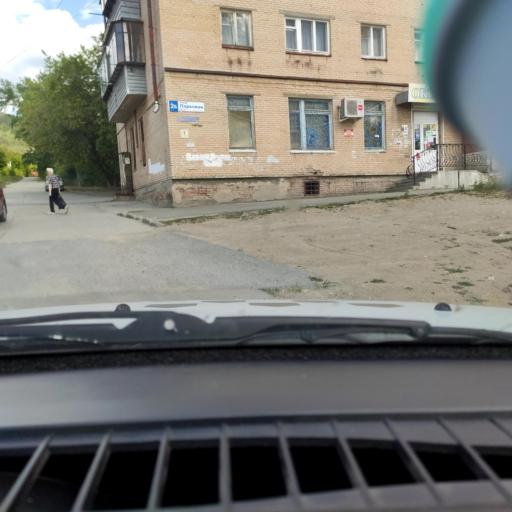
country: RU
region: Chelyabinsk
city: Miass
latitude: 55.0624
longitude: 60.1234
